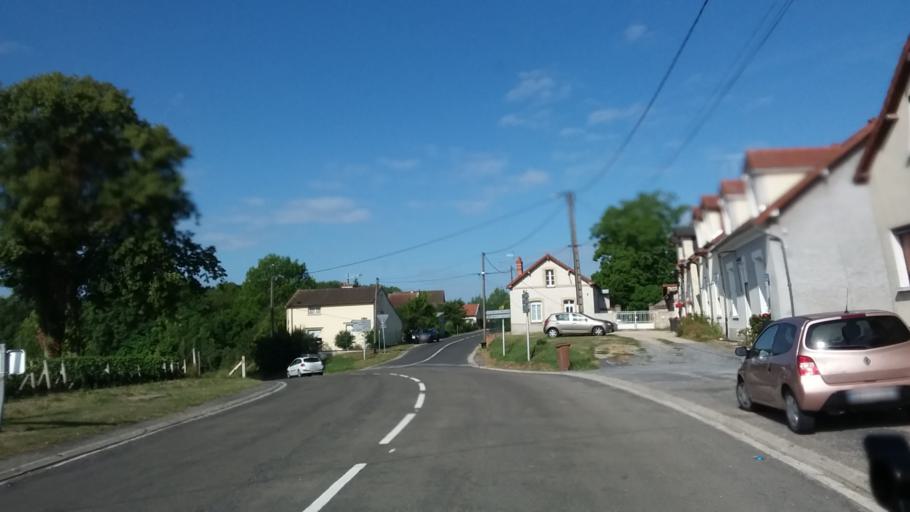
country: FR
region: Picardie
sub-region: Departement de l'Aisne
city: Saint-Erme-Outre-et-Ramecourt
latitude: 49.4617
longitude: 3.8197
